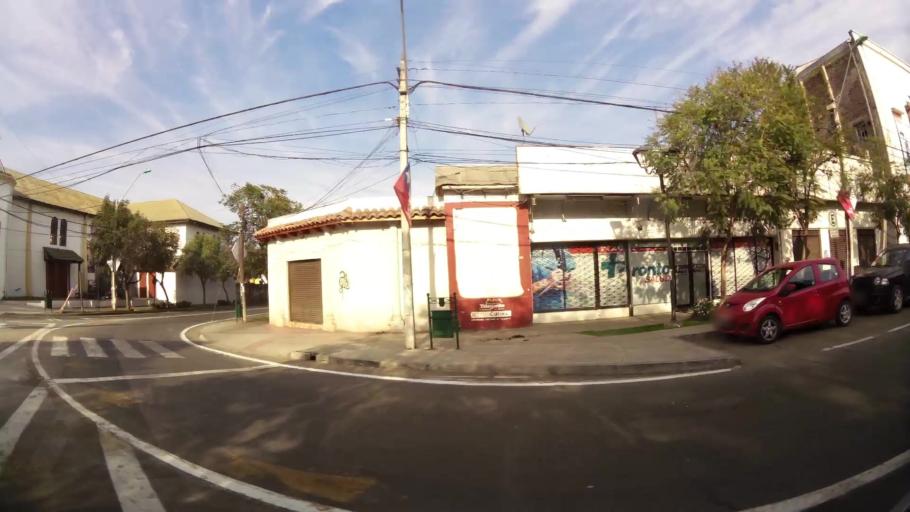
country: CL
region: Santiago Metropolitan
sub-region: Provincia de Talagante
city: Talagante
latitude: -33.6645
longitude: -70.9308
